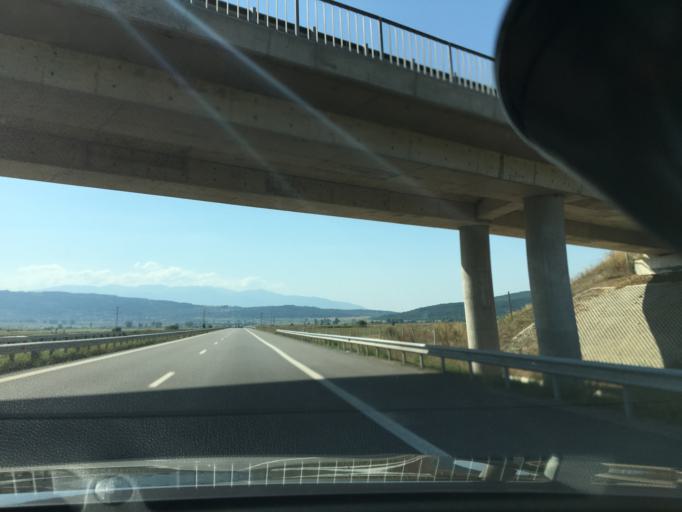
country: BG
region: Kyustendil
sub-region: Obshtina Bobovdol
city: Bobovdol
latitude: 42.4307
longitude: 23.1146
